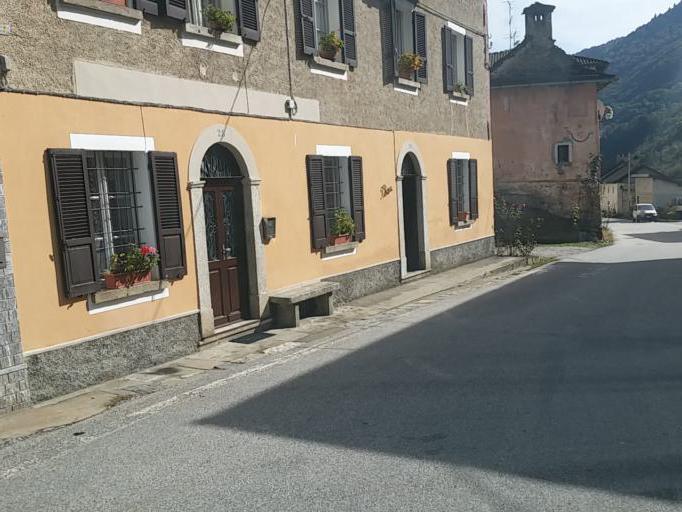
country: IT
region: Piedmont
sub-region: Provincia Verbano-Cusio-Ossola
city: Falmenta
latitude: 46.0718
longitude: 8.6064
